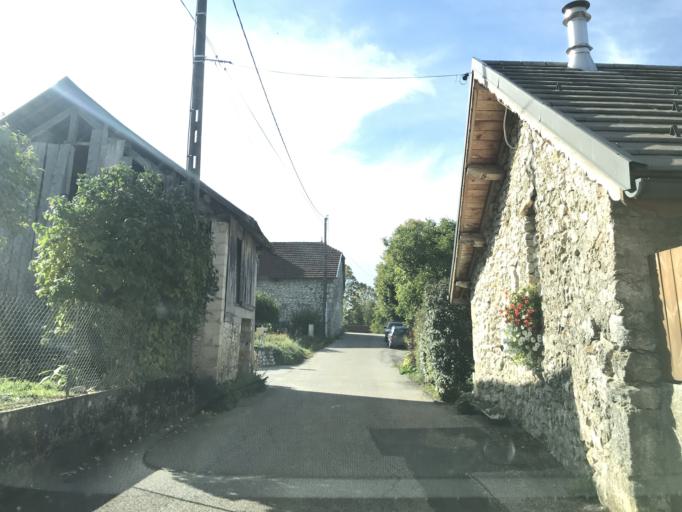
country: FR
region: Rhone-Alpes
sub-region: Departement de la Savoie
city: Novalaise
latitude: 45.6333
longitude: 5.8006
